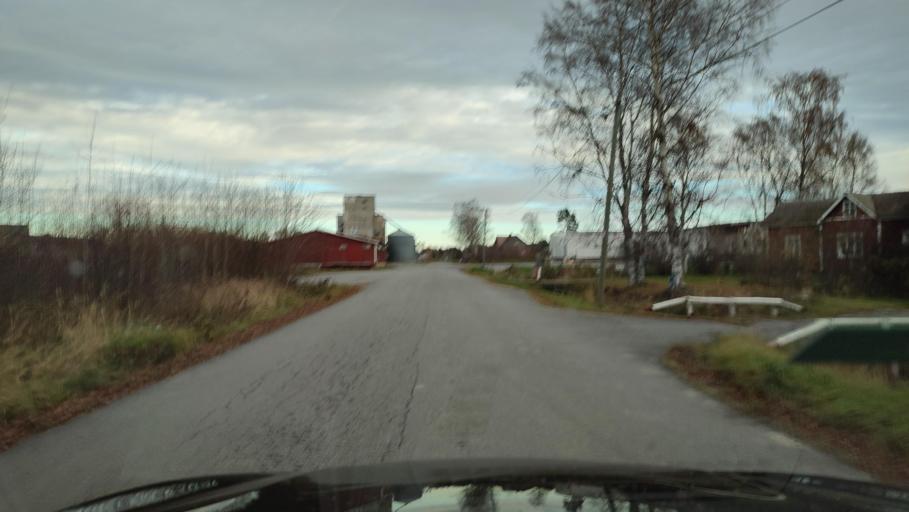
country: FI
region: Ostrobothnia
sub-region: Sydosterbotten
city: Naerpes
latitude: 62.4647
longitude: 21.3579
